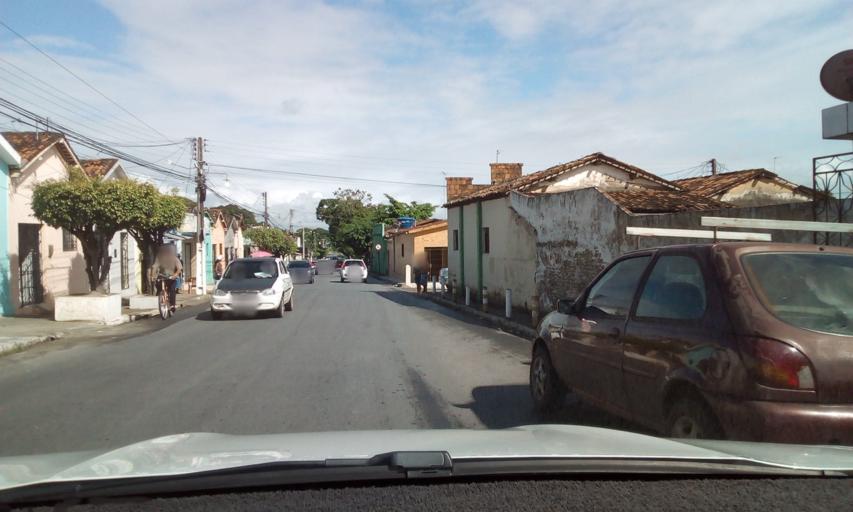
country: BR
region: Paraiba
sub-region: Santa Rita
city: Santa Rita
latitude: -7.1237
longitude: -34.9693
